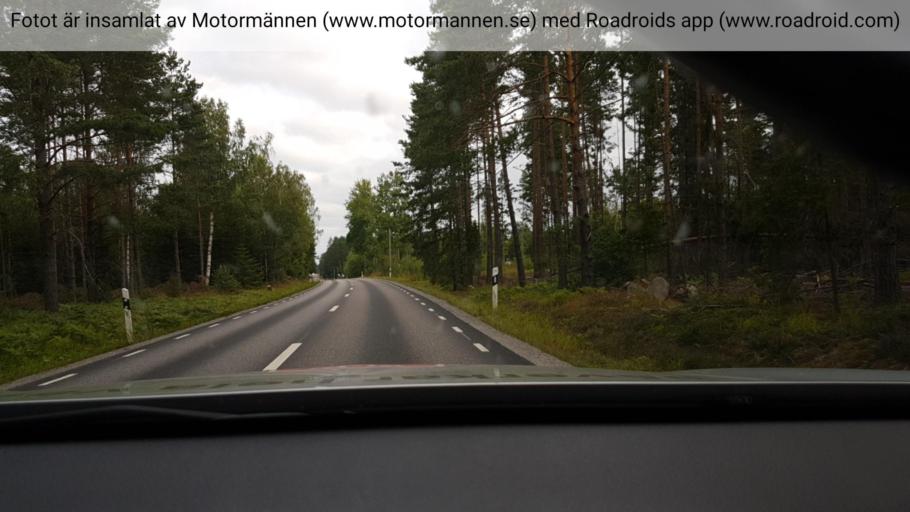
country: SE
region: Stockholm
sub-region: Norrtalje Kommun
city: Rimbo
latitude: 59.8061
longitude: 18.4408
